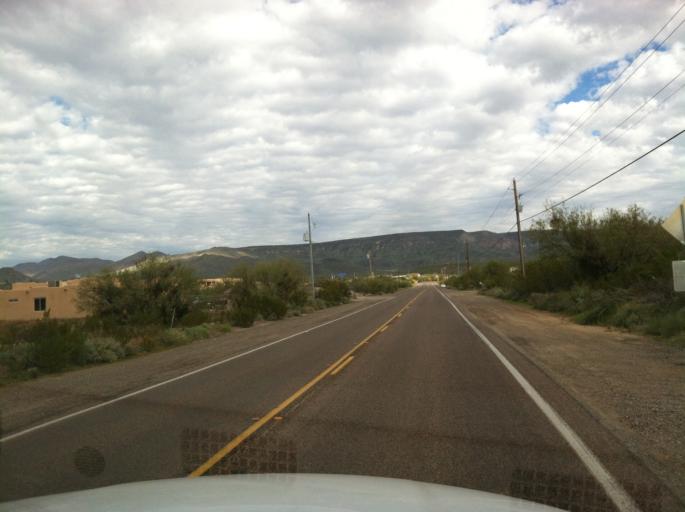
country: US
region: Arizona
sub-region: Maricopa County
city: New River
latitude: 33.9156
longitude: -112.0969
